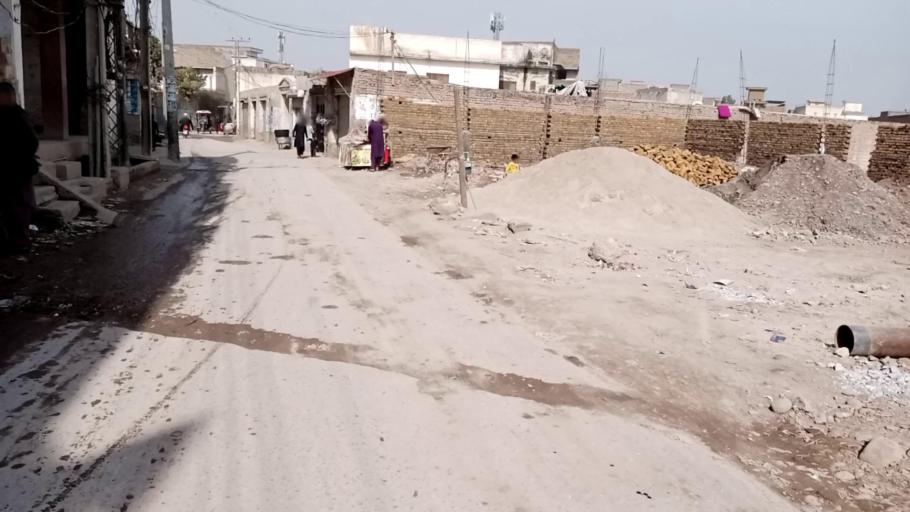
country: PK
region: Khyber Pakhtunkhwa
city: Peshawar
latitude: 33.9873
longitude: 71.4680
